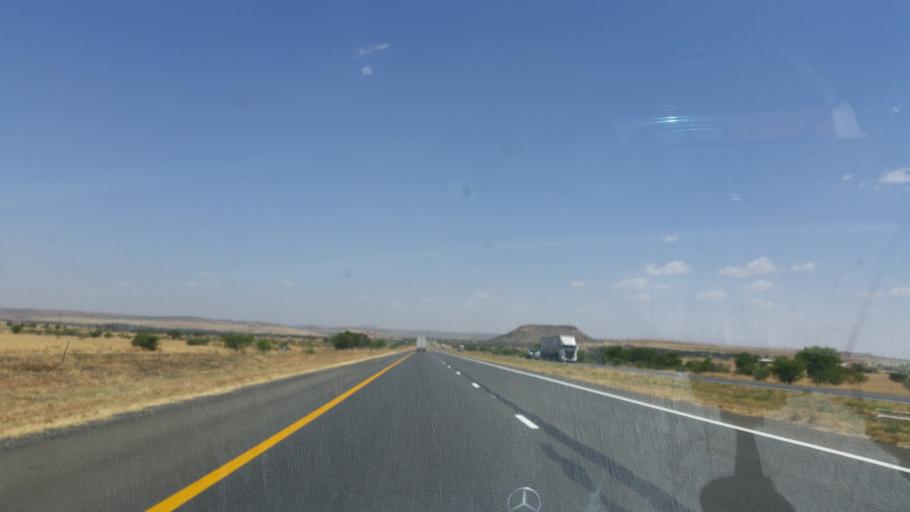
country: ZA
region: Orange Free State
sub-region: Lejweleputswa District Municipality
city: Brandfort
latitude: -28.9385
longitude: 26.4141
